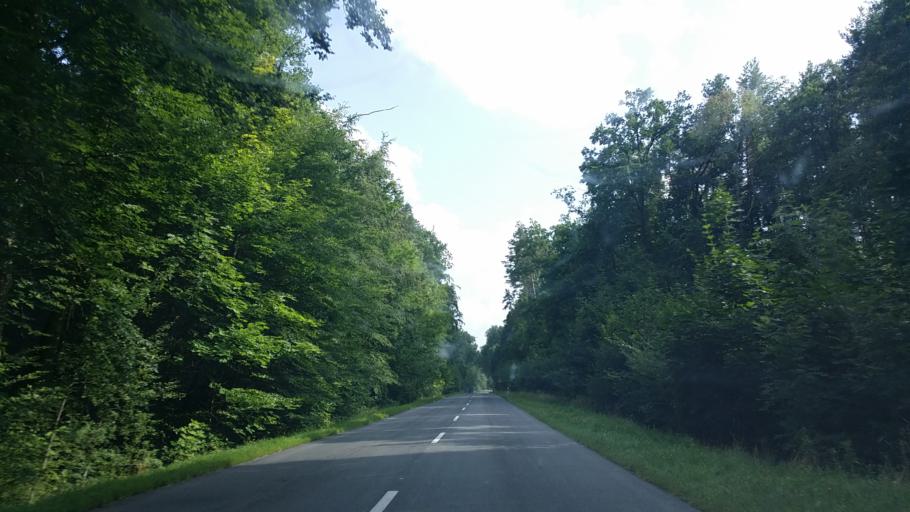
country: PL
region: Lubusz
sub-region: Powiat gorzowski
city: Klodawa
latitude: 52.8068
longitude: 15.2175
